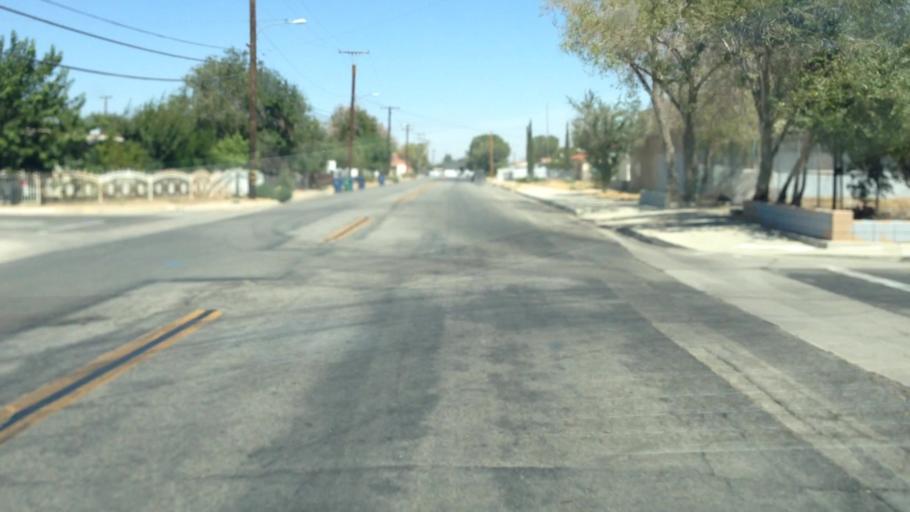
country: US
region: California
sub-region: Los Angeles County
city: Palmdale
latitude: 34.5830
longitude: -118.1143
